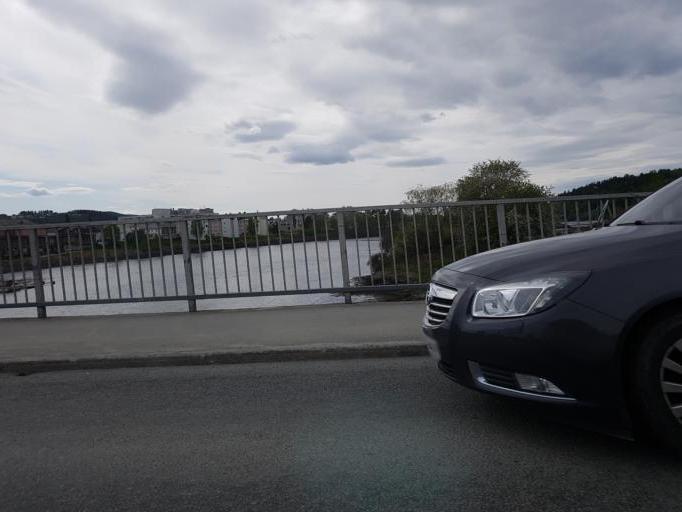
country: NO
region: Nord-Trondelag
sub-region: Levanger
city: Levanger
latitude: 63.7465
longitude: 11.2933
